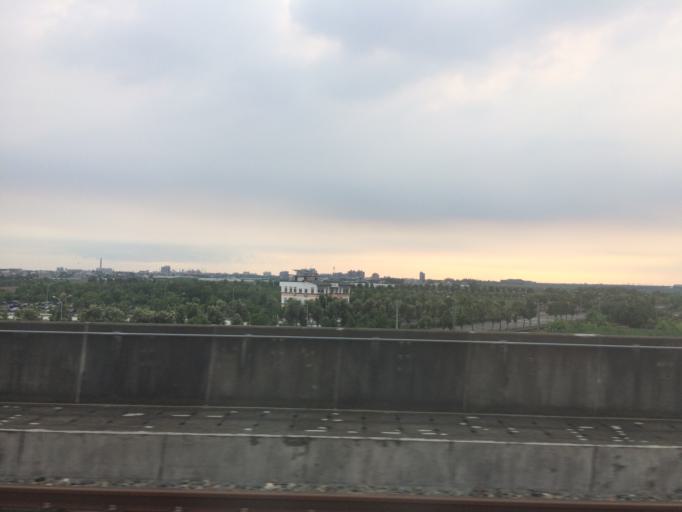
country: TW
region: Taiwan
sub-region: Chiayi
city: Taibao
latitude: 23.4636
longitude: 120.3240
